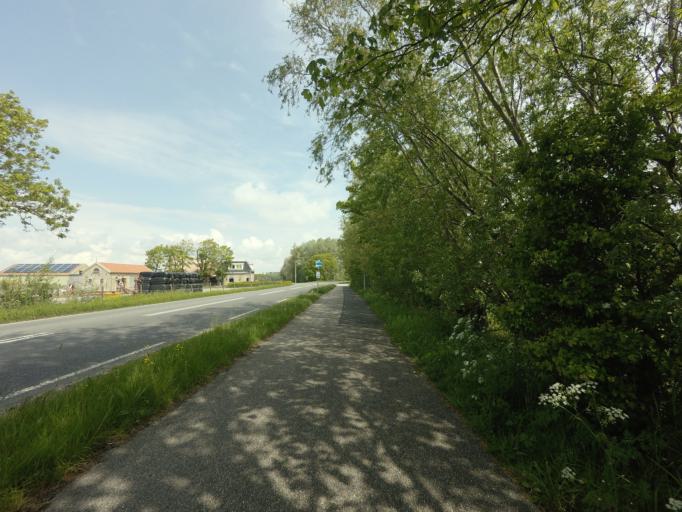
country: NL
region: Friesland
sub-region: Sudwest Fryslan
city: Bolsward
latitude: 53.1104
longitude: 5.4803
